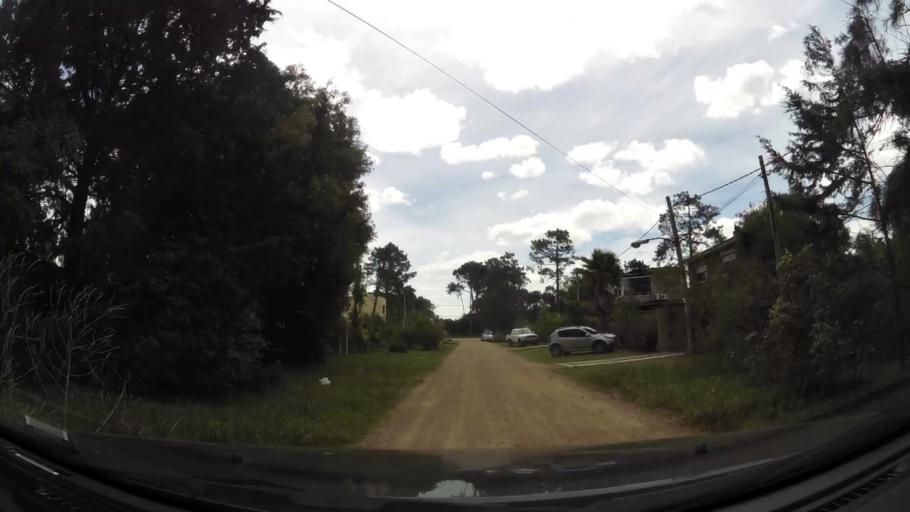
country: UY
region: Canelones
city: Empalme Olmos
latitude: -34.7976
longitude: -55.8938
